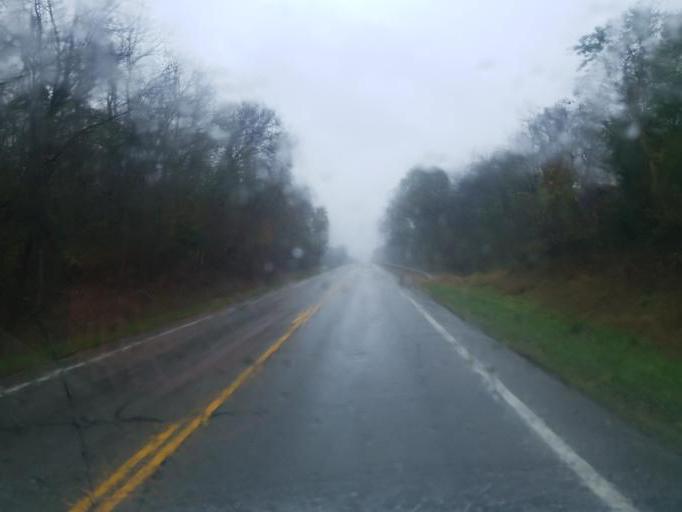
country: US
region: Ohio
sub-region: Muskingum County
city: North Zanesville
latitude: 39.9992
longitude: -82.0763
